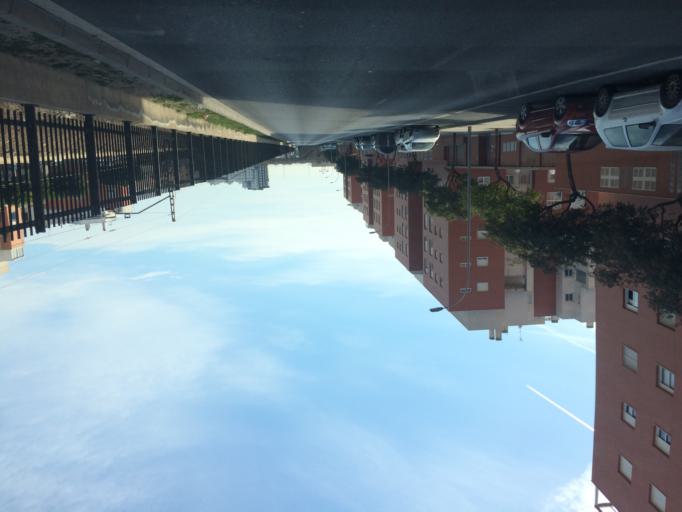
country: ES
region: Andalusia
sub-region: Provincia de Almeria
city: Almeria
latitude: 36.8465
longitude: -2.4356
